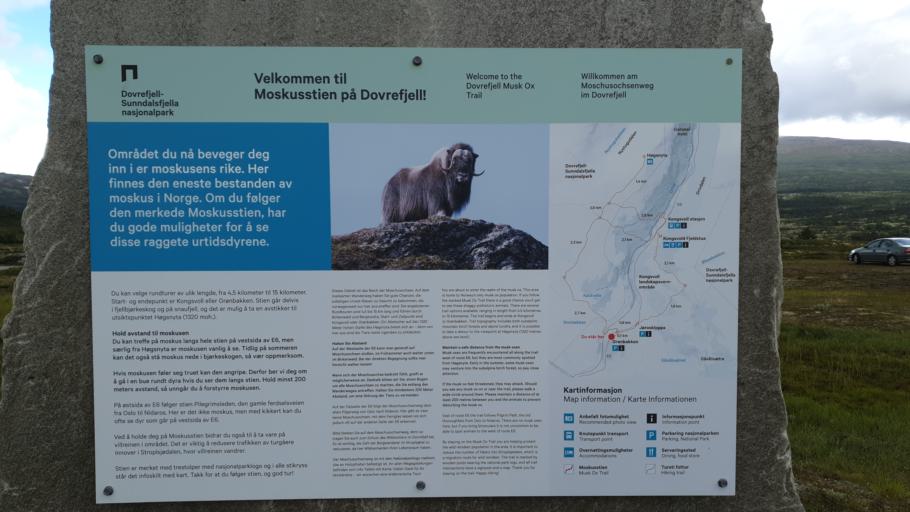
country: NO
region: Sor-Trondelag
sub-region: Oppdal
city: Oppdal
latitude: 62.2766
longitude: 9.5870
